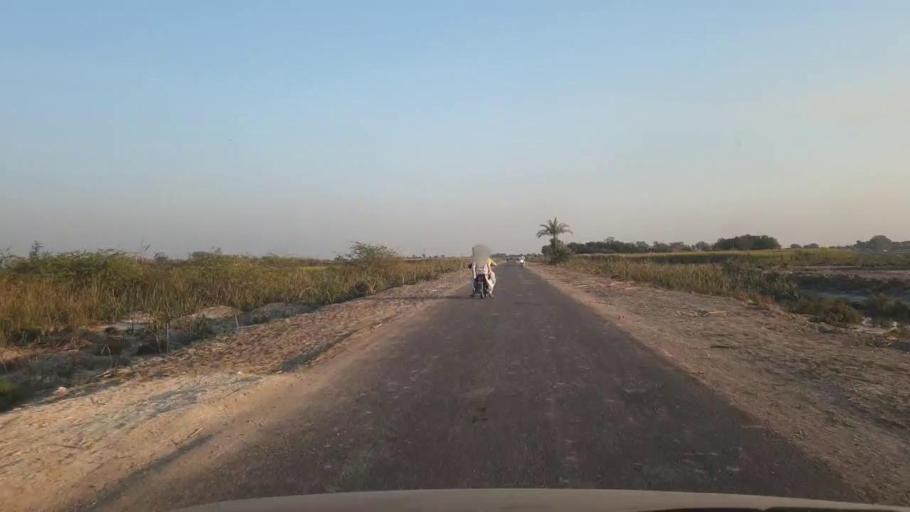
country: PK
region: Sindh
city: Chambar
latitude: 25.2808
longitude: 68.9128
